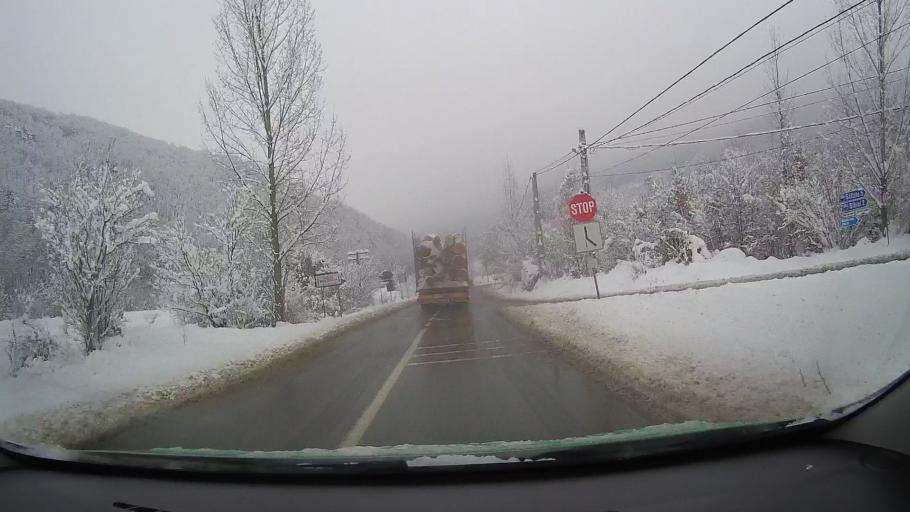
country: RO
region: Sibiu
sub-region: Comuna Orlat
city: Orlat
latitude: 45.7644
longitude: 23.9405
